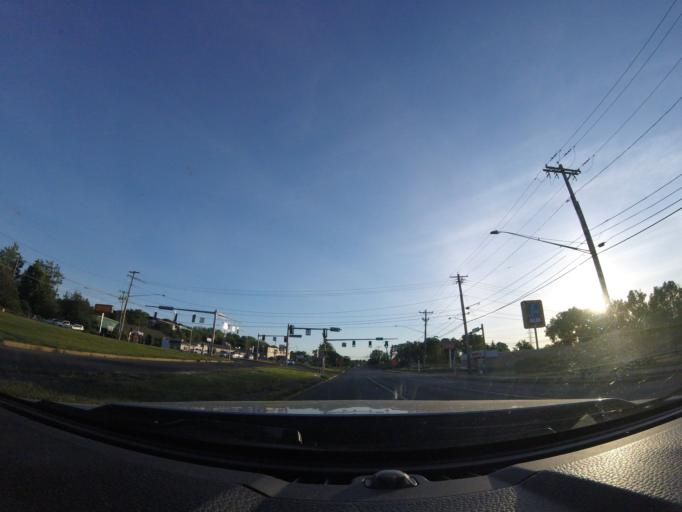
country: US
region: New York
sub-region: Onondaga County
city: Syracuse
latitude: 43.0500
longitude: -76.1167
